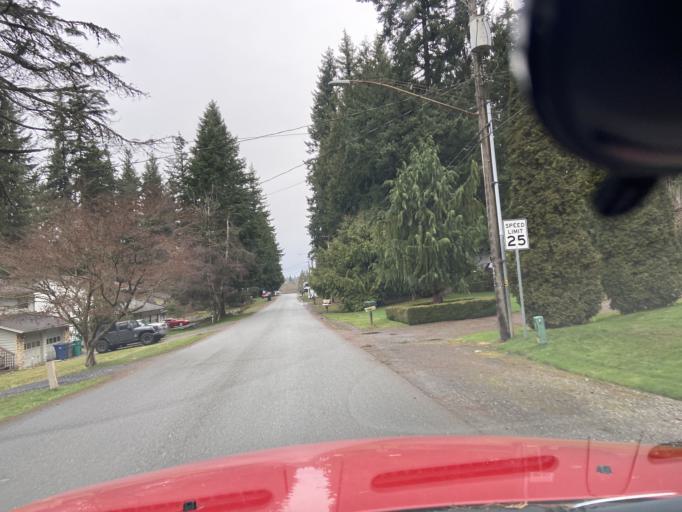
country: US
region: Washington
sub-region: Snohomish County
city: Fobes Hill
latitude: 47.9641
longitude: -122.1005
